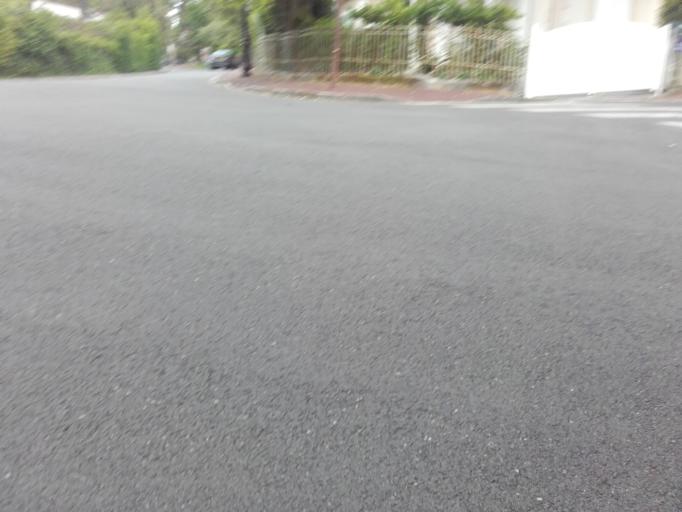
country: FR
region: Aquitaine
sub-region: Departement de la Gironde
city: Arcachon
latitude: 44.6570
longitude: -1.1775
